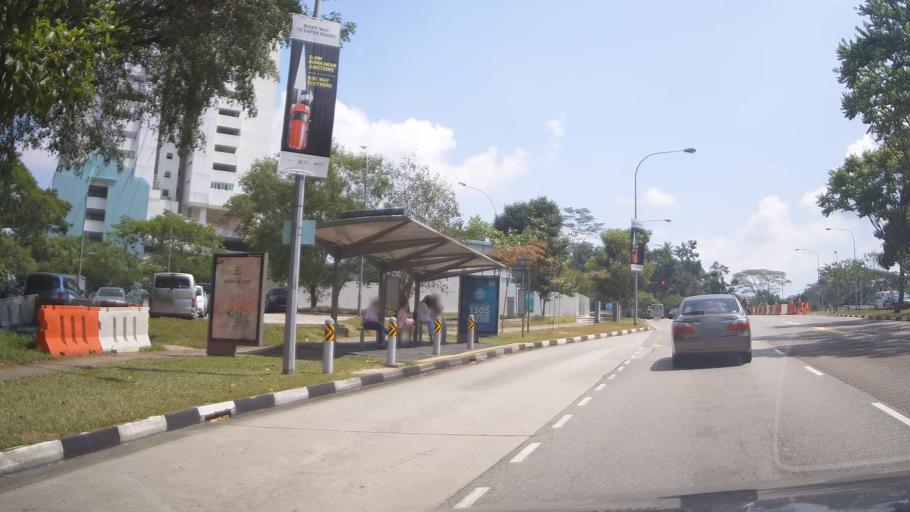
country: SG
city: Singapore
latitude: 1.3408
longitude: 103.7768
